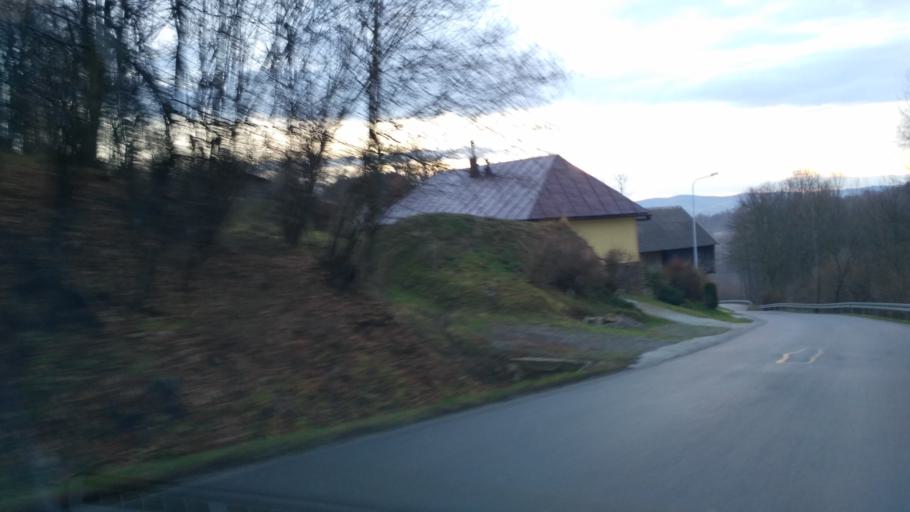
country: PL
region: Subcarpathian Voivodeship
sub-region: Powiat strzyzowski
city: Polomia
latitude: 49.8759
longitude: 21.8627
